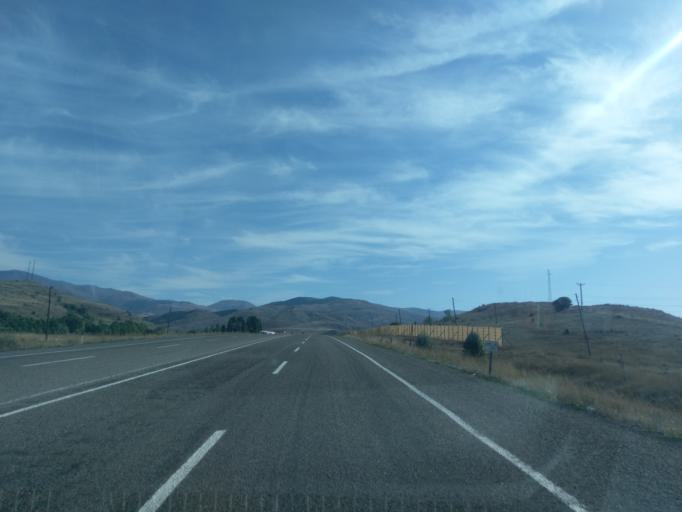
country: TR
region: Sivas
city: Imranli
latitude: 39.8357
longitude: 38.2700
